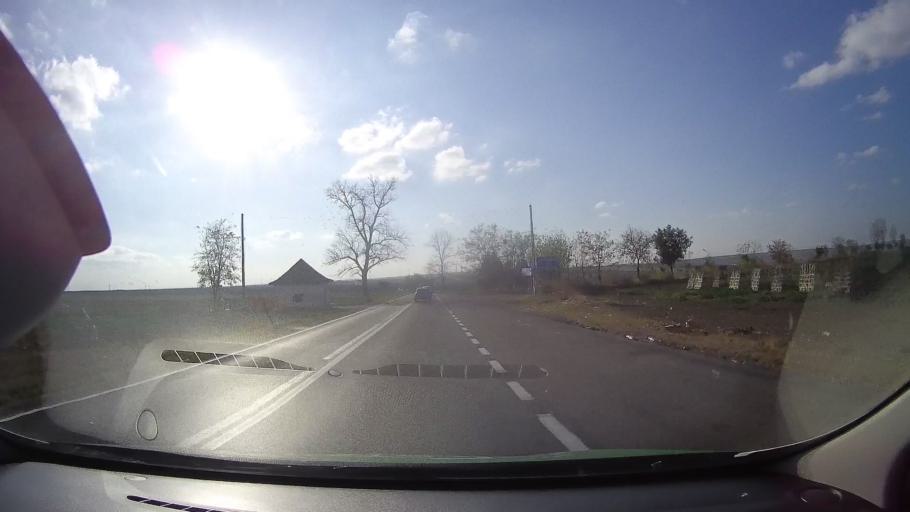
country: RO
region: Tulcea
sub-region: Comuna Topolog
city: Topolog
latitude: 44.8478
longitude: 28.3190
